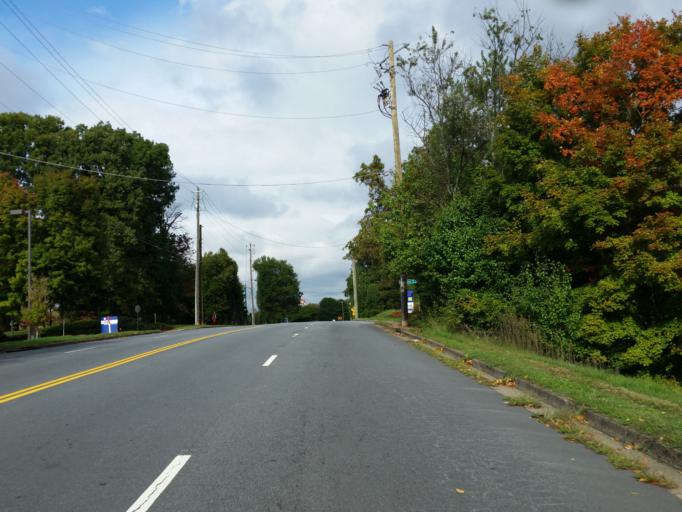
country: US
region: Georgia
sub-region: Cobb County
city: Smyrna
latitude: 33.9182
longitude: -84.4940
